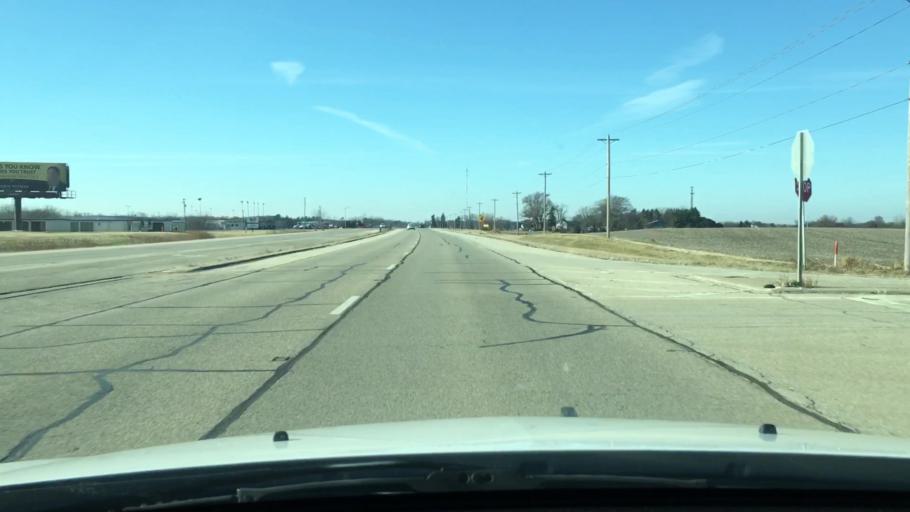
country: US
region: Illinois
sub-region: Woodford County
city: Germantown Hills
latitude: 40.7751
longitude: -89.4274
